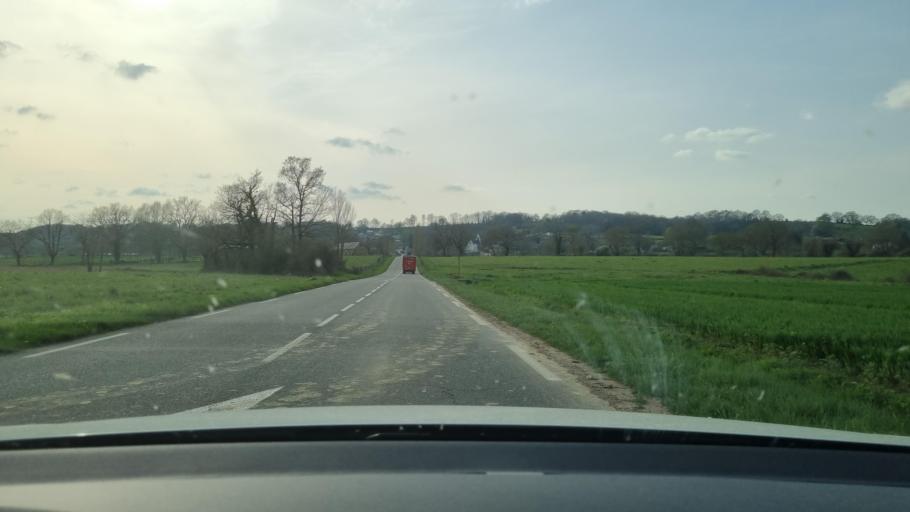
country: FR
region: Aquitaine
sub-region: Departement des Pyrenees-Atlantiques
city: Soumoulou
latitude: 43.3775
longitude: -0.1211
